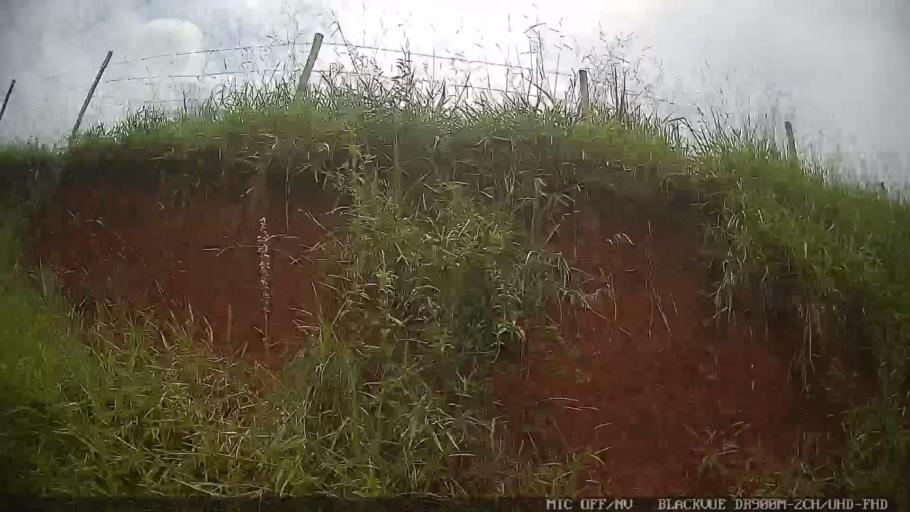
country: BR
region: Sao Paulo
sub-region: Santa Isabel
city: Santa Isabel
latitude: -23.3434
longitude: -46.2271
